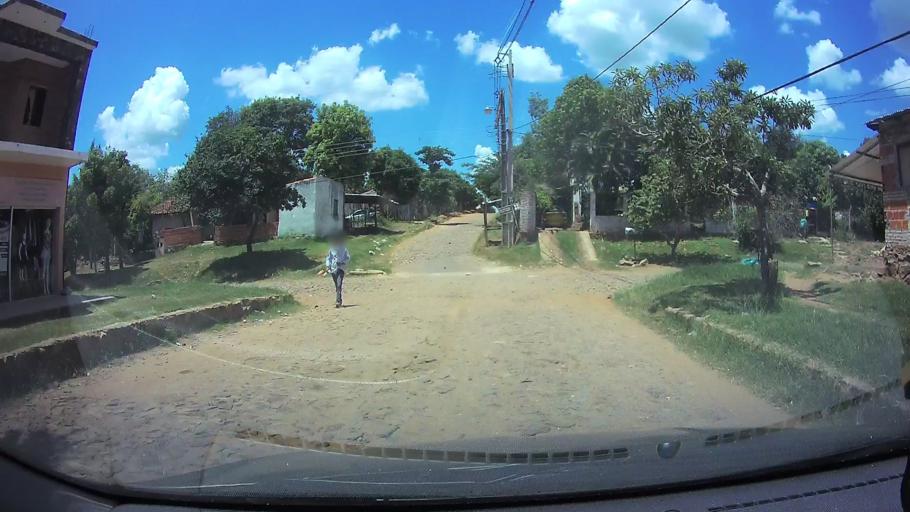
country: PY
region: Central
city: Limpio
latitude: -25.1530
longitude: -57.4464
